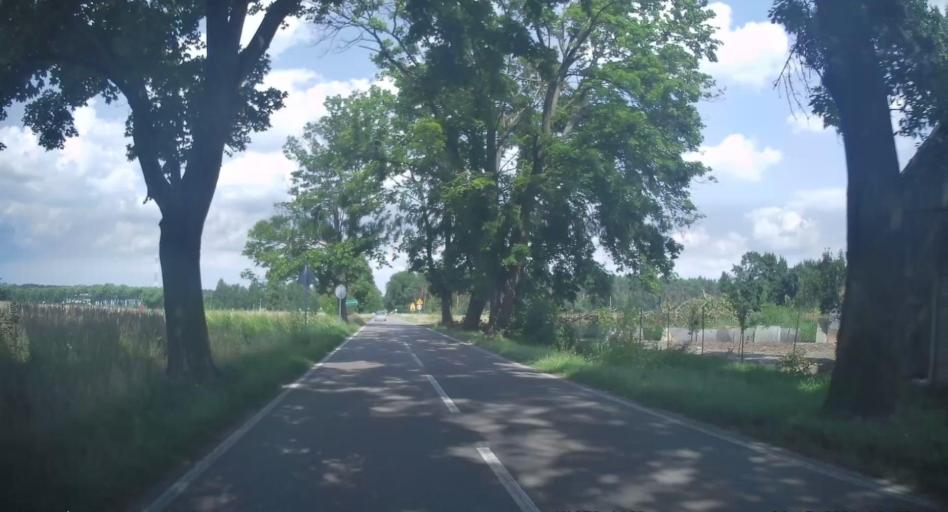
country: PL
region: Lodz Voivodeship
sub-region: Powiat tomaszowski
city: Lubochnia
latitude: 51.5735
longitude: 20.0965
